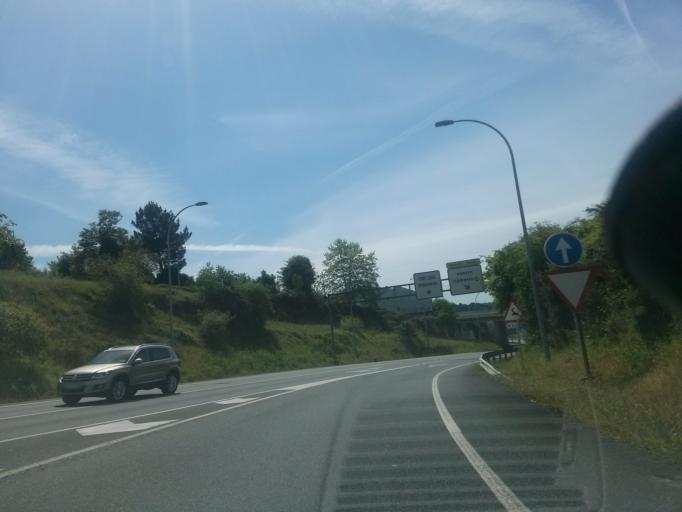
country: ES
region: Galicia
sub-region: Provincia de Lugo
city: Lugo
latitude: 43.0088
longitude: -7.5741
